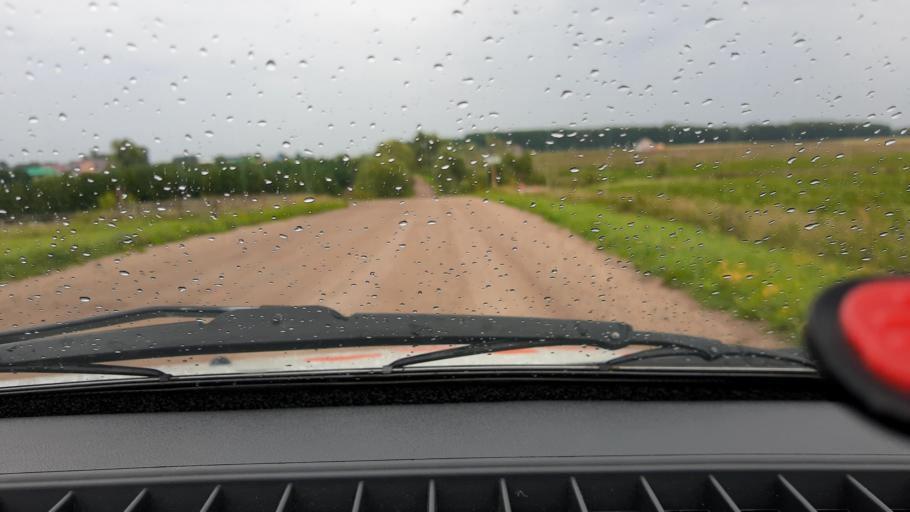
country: RU
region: Bashkortostan
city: Karmaskaly
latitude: 54.3840
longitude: 56.1163
